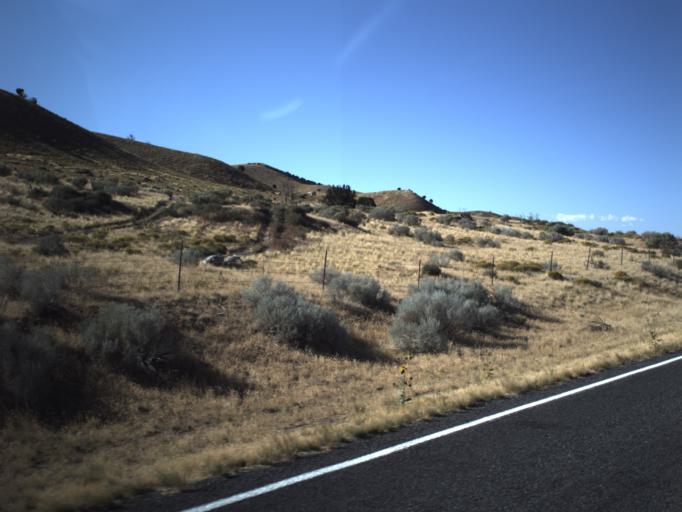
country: US
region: Utah
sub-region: Millard County
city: Delta
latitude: 39.4535
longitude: -112.3037
